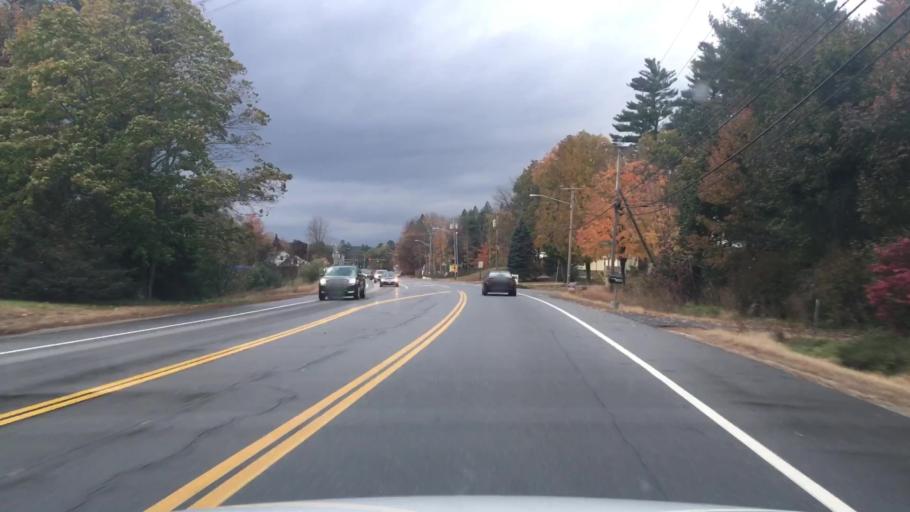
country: US
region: New Hampshire
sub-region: Merrimack County
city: Epsom
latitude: 43.2241
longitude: -71.3413
